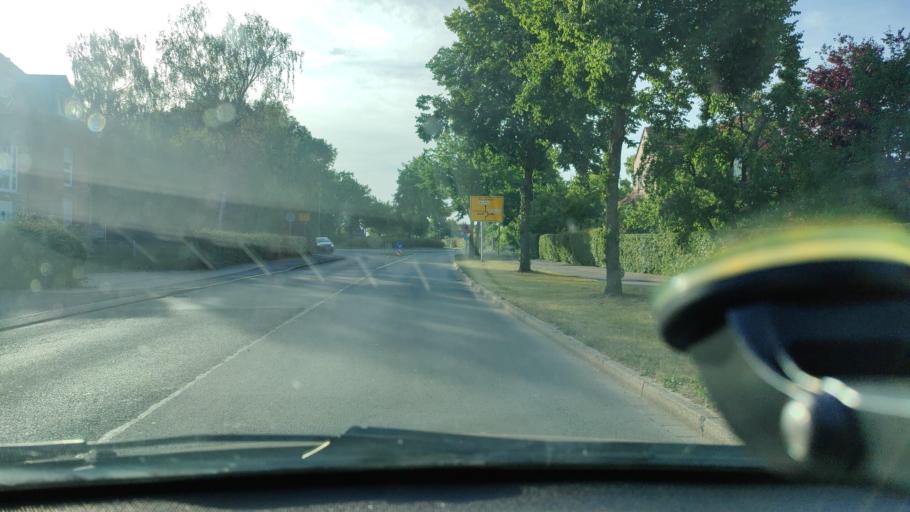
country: DE
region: North Rhine-Westphalia
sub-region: Regierungsbezirk Munster
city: Billerbeck
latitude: 51.9804
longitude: 7.2781
